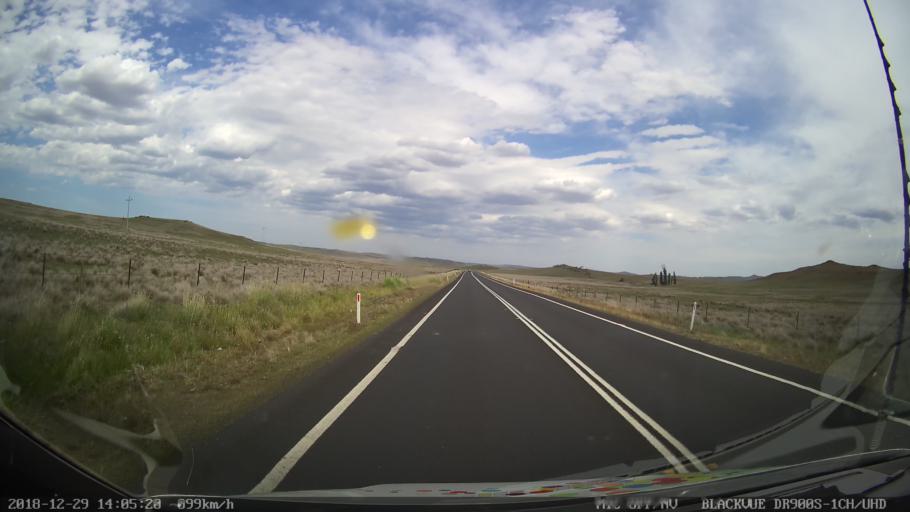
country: AU
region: New South Wales
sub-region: Cooma-Monaro
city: Cooma
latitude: -36.3291
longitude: 149.1908
